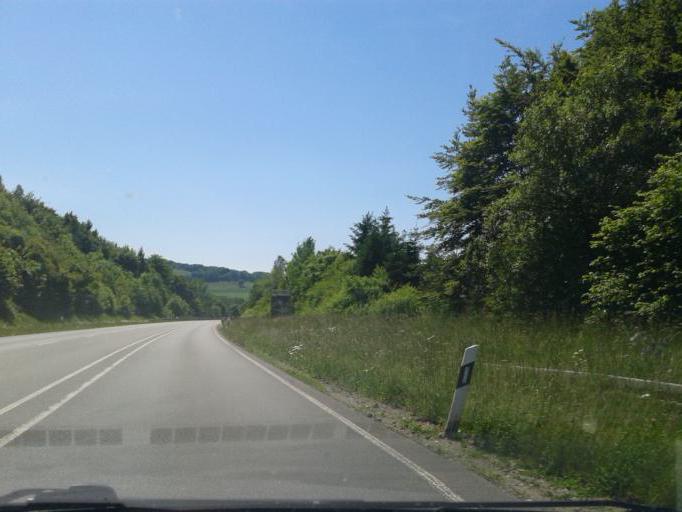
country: DE
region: North Rhine-Westphalia
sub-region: Regierungsbezirk Detmold
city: Bad Meinberg
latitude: 51.8910
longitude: 9.0064
